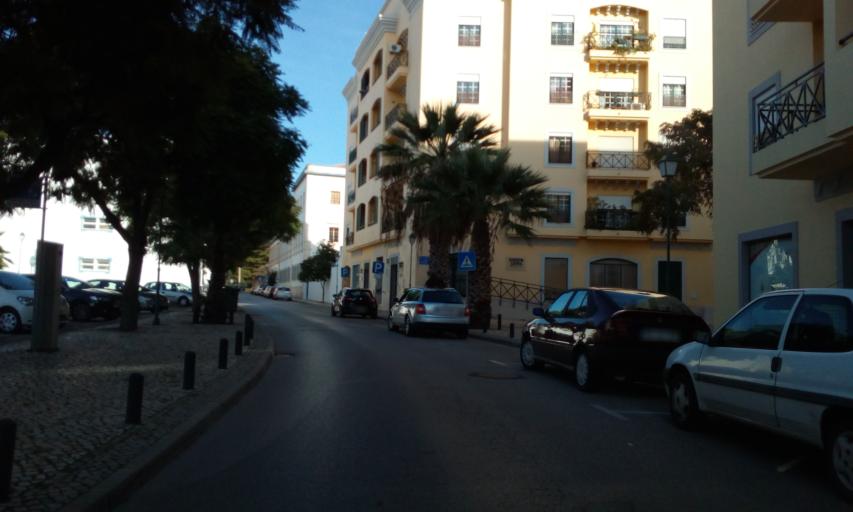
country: PT
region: Faro
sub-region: Faro
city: Faro
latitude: 37.0144
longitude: -7.9297
